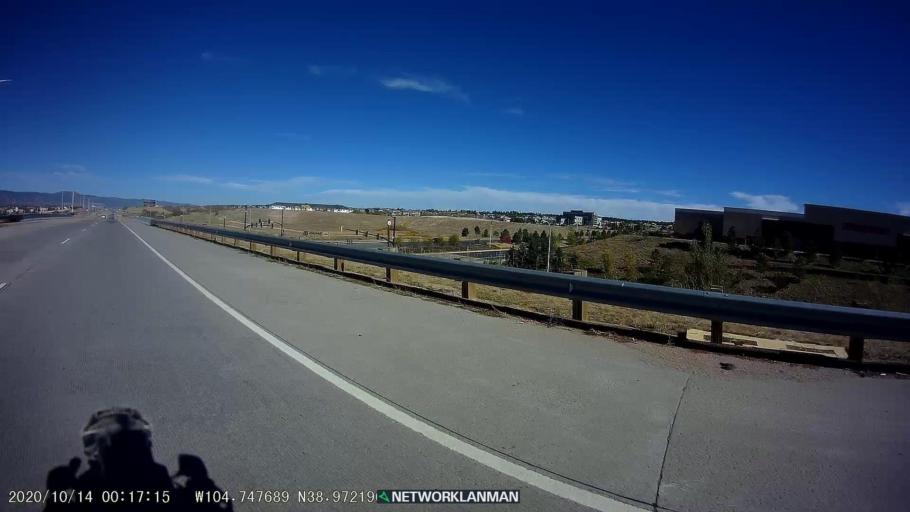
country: US
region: Colorado
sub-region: El Paso County
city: Black Forest
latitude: 38.9725
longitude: -104.7482
